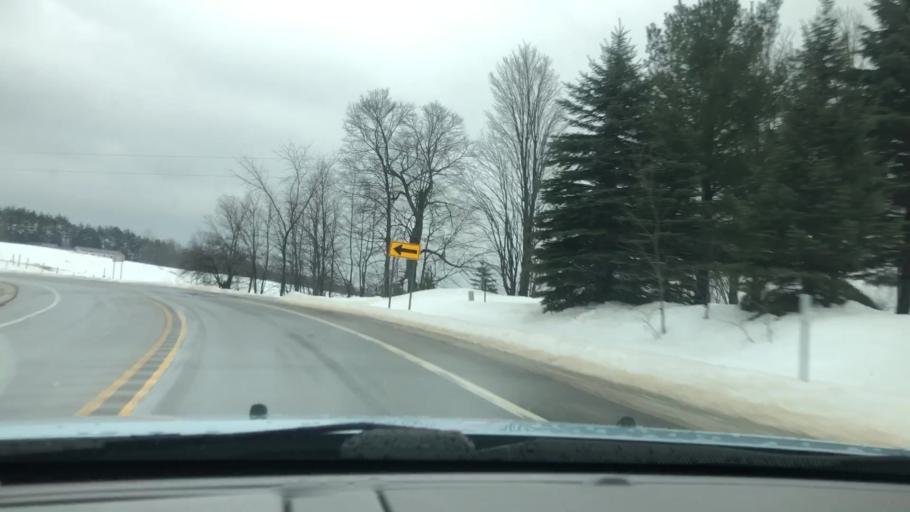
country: US
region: Michigan
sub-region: Charlevoix County
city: East Jordan
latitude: 45.0967
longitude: -85.0242
